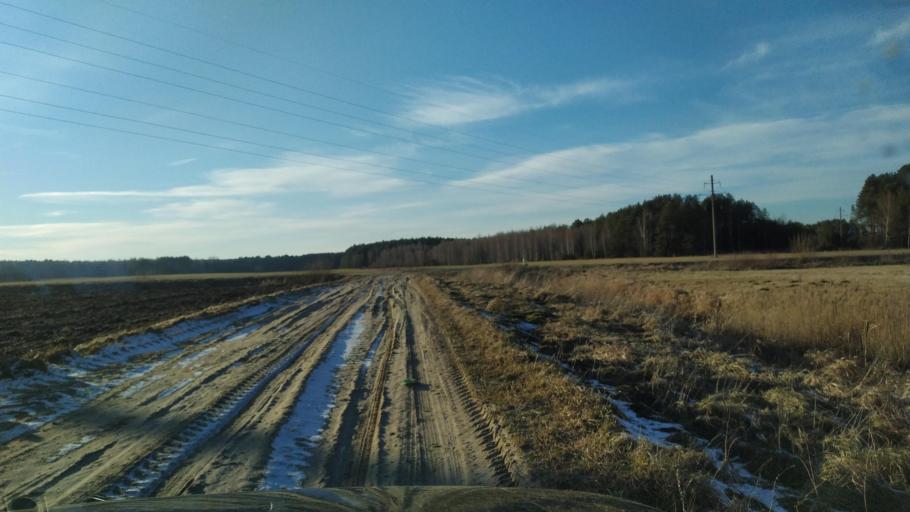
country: BY
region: Brest
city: Pruzhany
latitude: 52.5537
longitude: 24.2968
